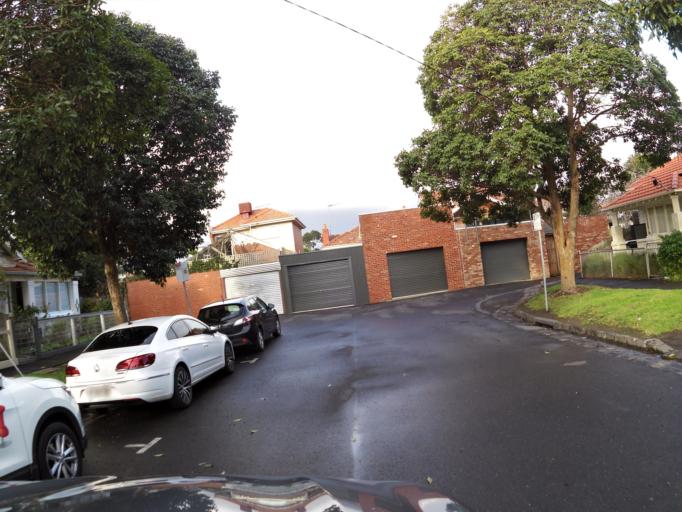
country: AU
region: Victoria
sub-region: Yarra
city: Richmond
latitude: -37.8118
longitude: 145.0056
